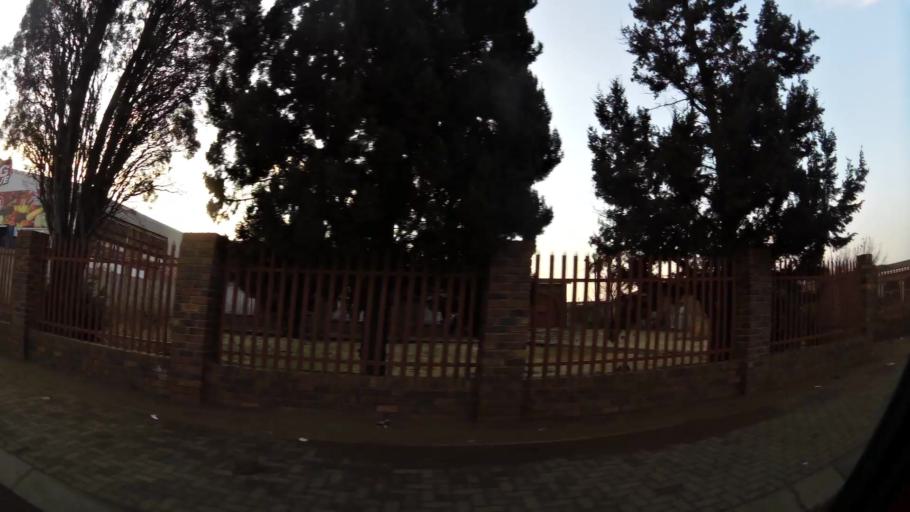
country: ZA
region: Gauteng
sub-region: City of Johannesburg Metropolitan Municipality
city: Orange Farm
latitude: -26.5369
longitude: 27.8339
